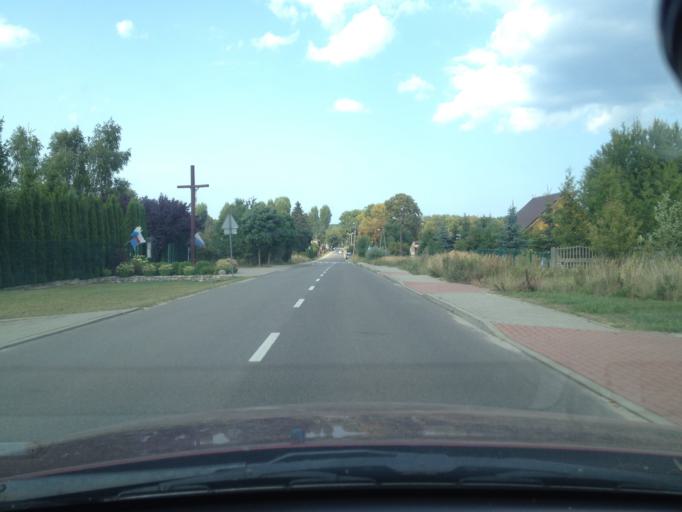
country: PL
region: West Pomeranian Voivodeship
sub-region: Powiat gryficki
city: Pobierowo
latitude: 54.0389
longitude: 14.8739
